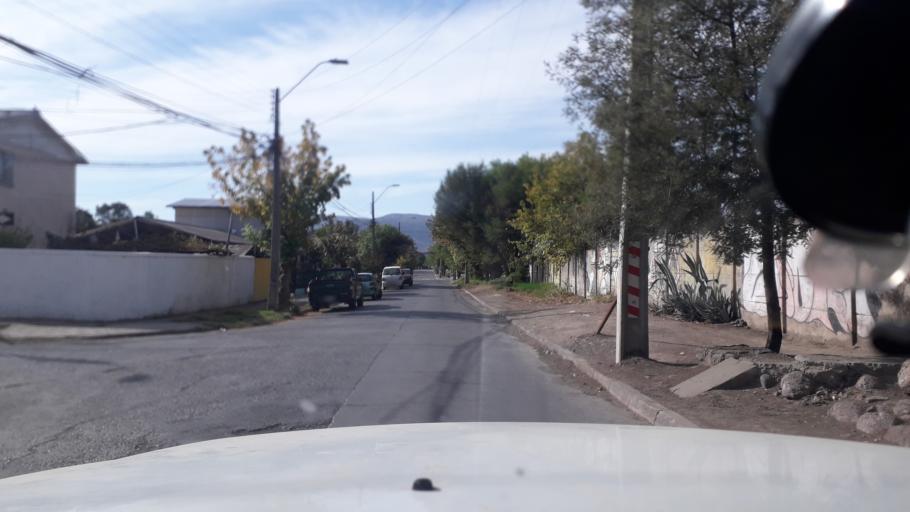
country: CL
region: Valparaiso
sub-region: Provincia de San Felipe
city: San Felipe
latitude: -32.7537
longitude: -70.7163
